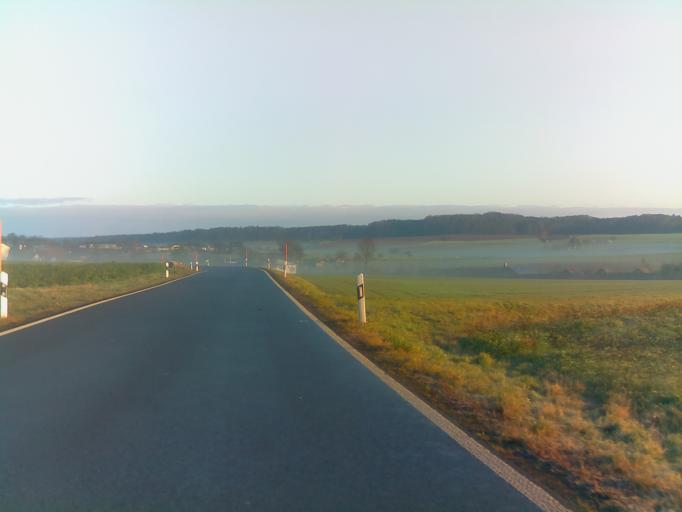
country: DE
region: Bavaria
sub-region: Regierungsbezirk Unterfranken
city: Neunkirchen
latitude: 49.6994
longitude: 9.4002
